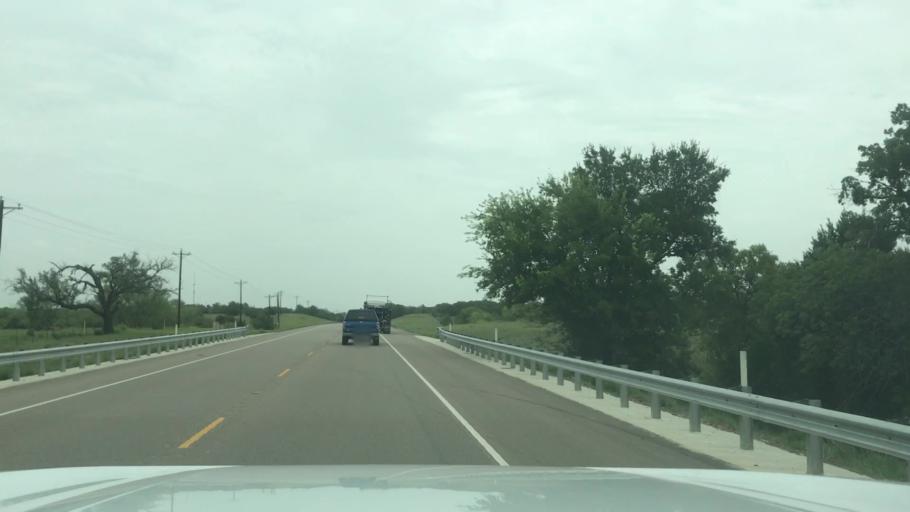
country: US
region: Texas
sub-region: Bosque County
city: Meridian
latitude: 31.9274
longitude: -97.6871
